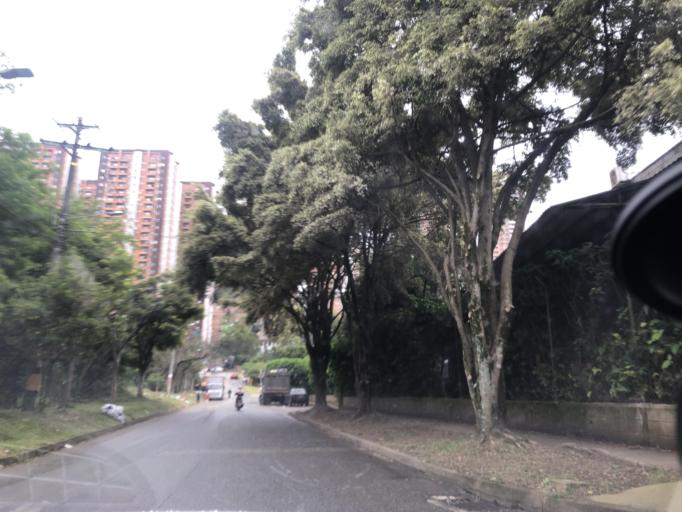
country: CO
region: Antioquia
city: Bello
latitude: 6.3249
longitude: -75.5499
